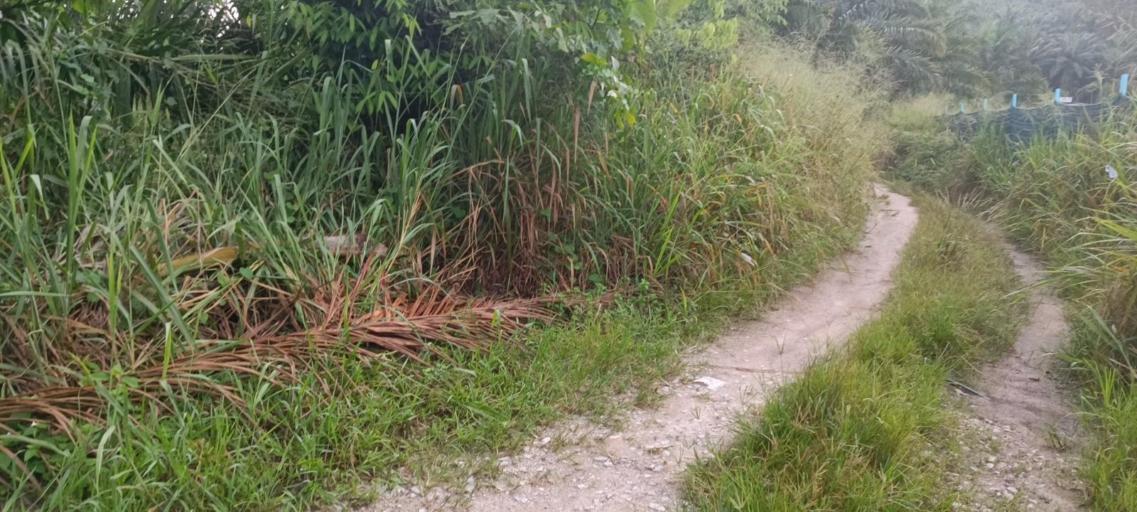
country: MY
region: Penang
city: Nibong Tebal
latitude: 5.2319
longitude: 100.5051
